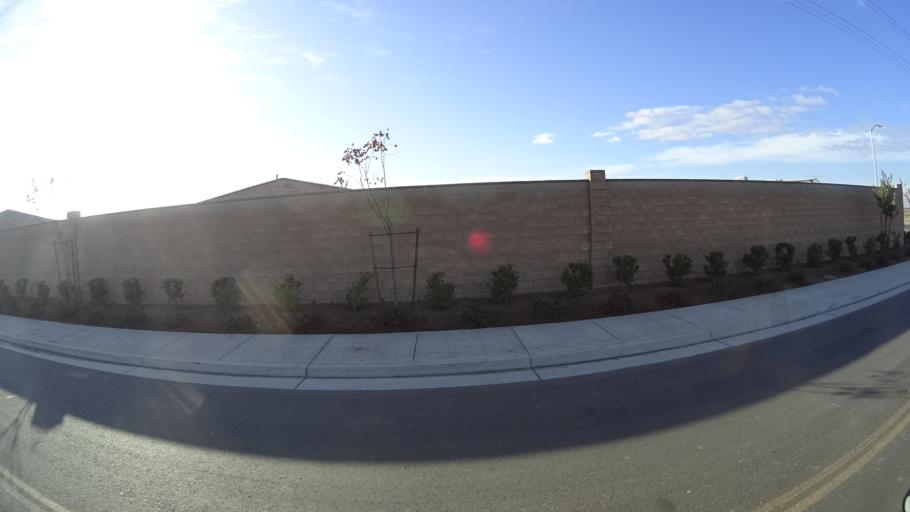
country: US
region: California
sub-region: Kern County
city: Rosedale
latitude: 35.3034
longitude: -119.1452
